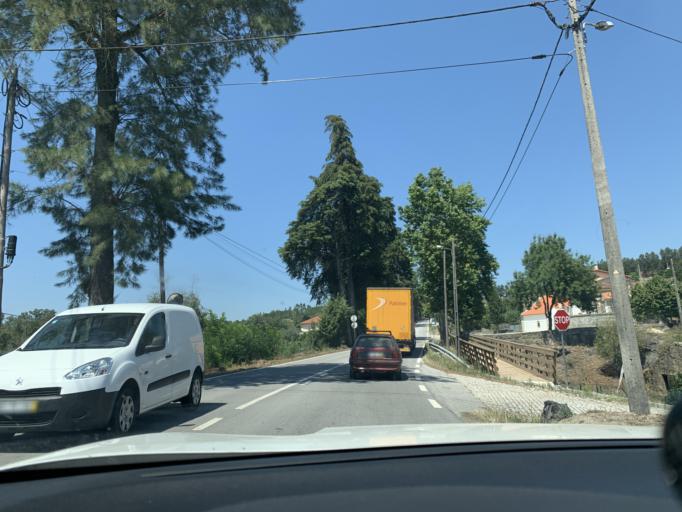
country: PT
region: Viseu
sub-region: Mangualde
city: Mangualde
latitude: 40.5923
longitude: -7.8005
